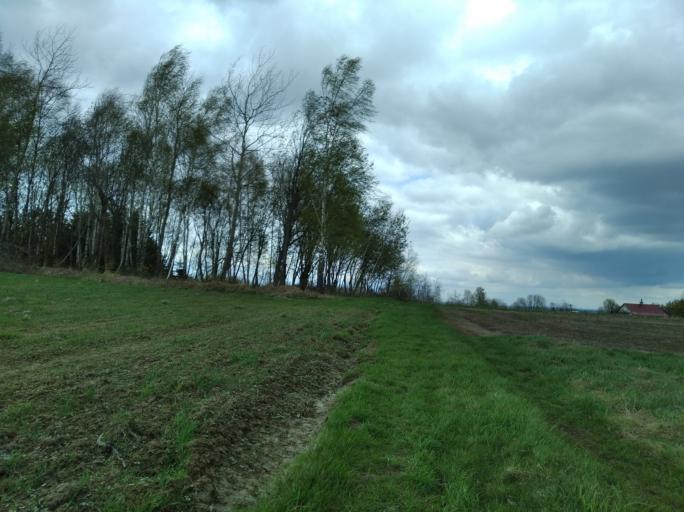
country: PL
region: Subcarpathian Voivodeship
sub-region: Powiat strzyzowski
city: Niebylec
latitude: 49.8865
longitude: 21.9333
